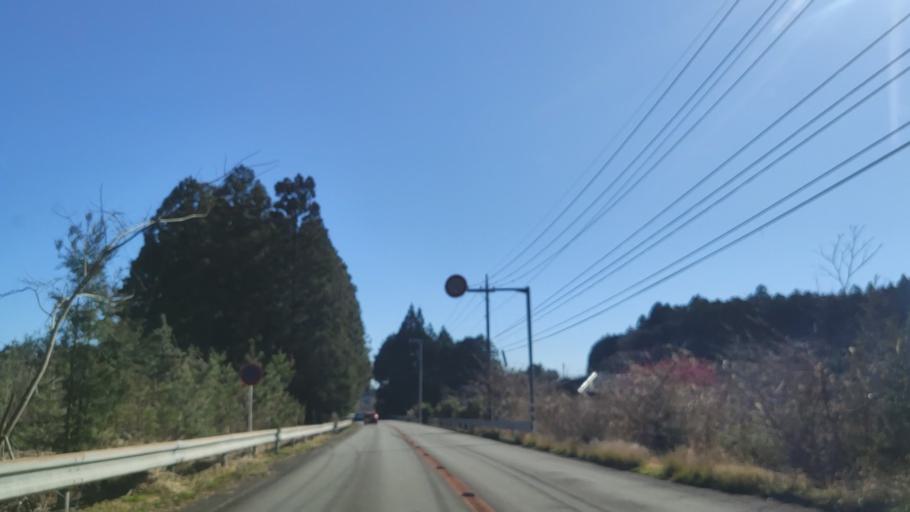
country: JP
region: Shizuoka
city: Fujinomiya
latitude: 35.3224
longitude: 138.5861
